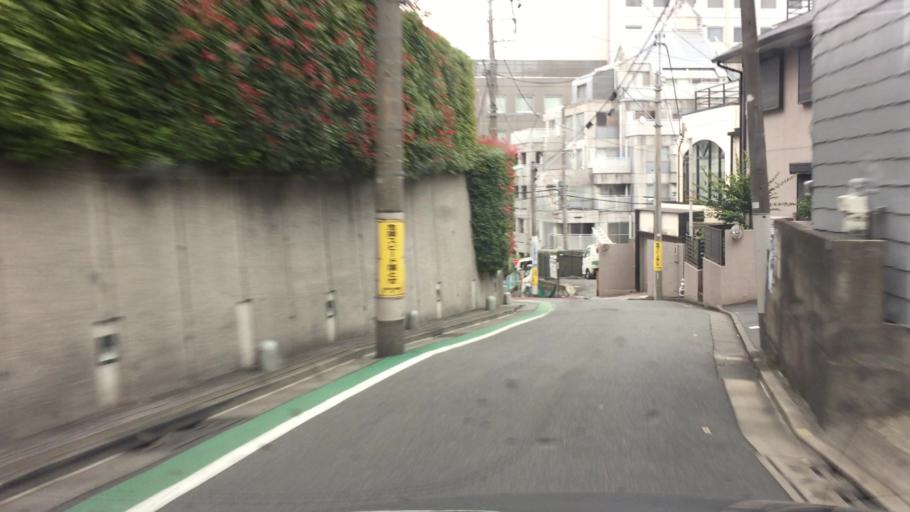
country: JP
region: Tokyo
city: Tokyo
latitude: 35.6479
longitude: 139.6913
